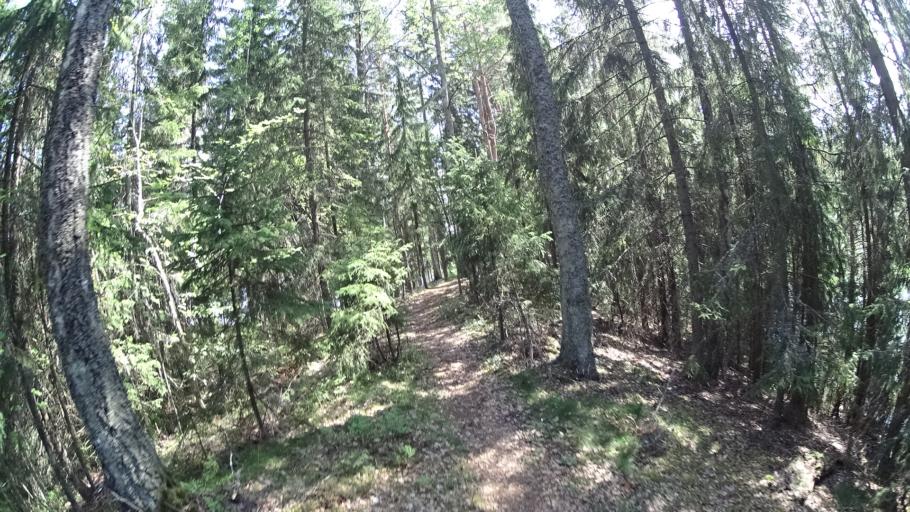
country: FI
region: Haeme
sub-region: Forssa
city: Tammela
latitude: 60.7683
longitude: 23.8802
